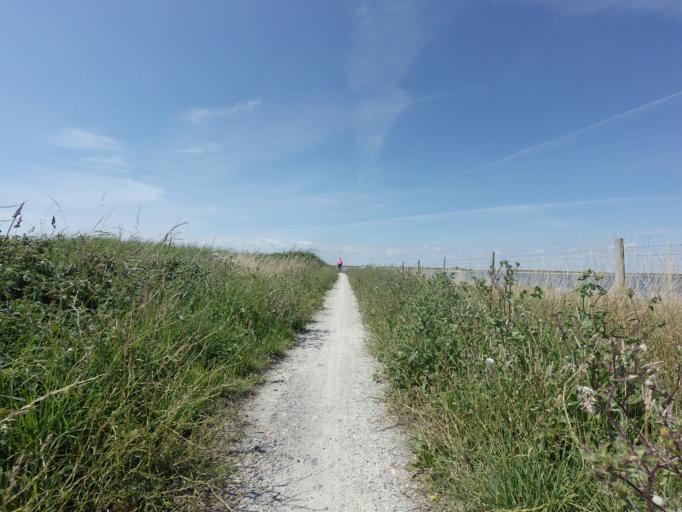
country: GB
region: England
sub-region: Kent
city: Lydd
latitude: 50.9340
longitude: 0.8594
